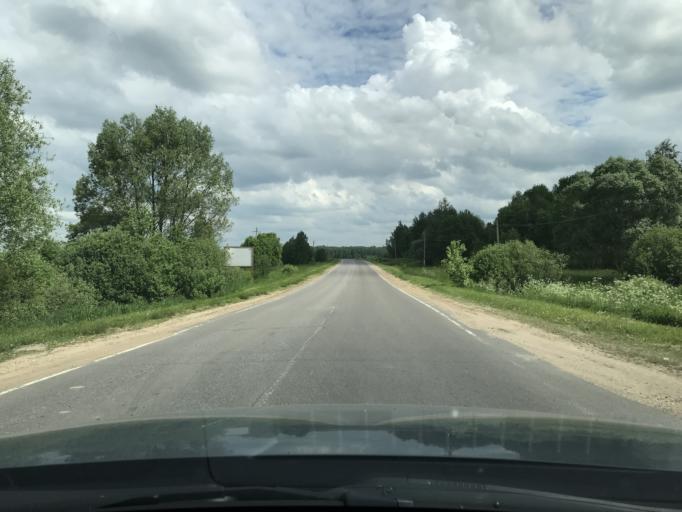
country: RU
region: Kaluga
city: Borovsk
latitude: 55.3572
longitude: 36.3973
